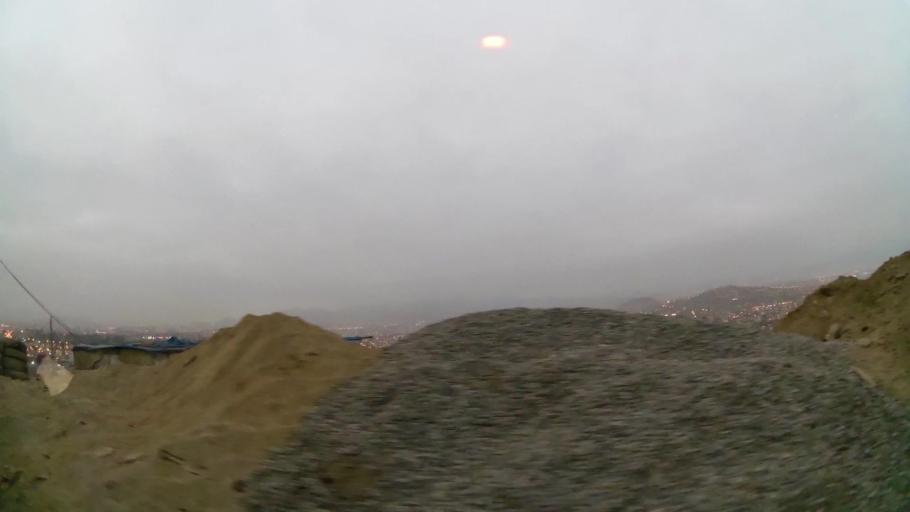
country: PE
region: Lima
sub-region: Lima
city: Surco
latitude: -12.1856
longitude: -77.0209
